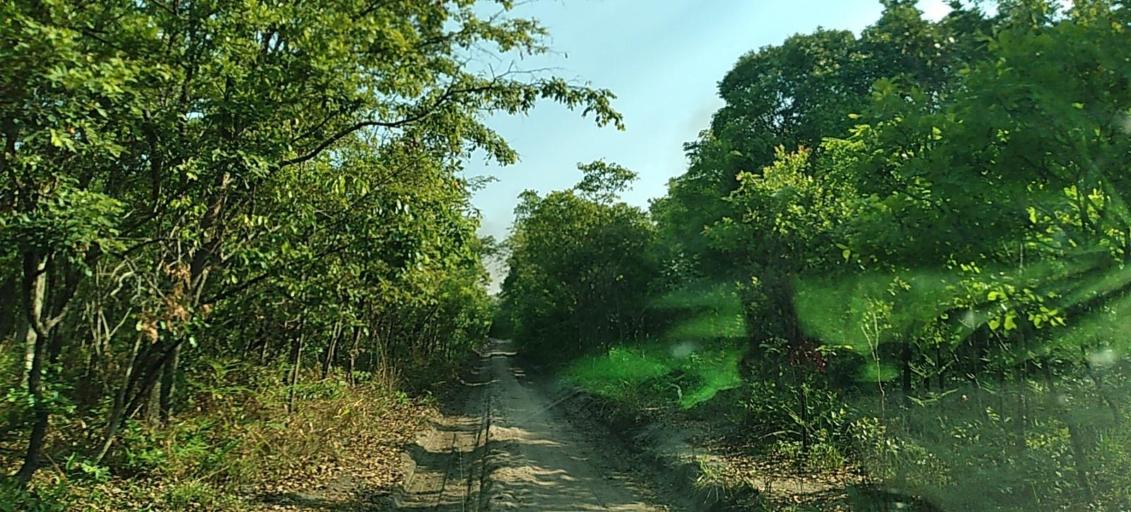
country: ZM
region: North-Western
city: Mwinilunga
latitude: -11.3207
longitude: 24.7391
